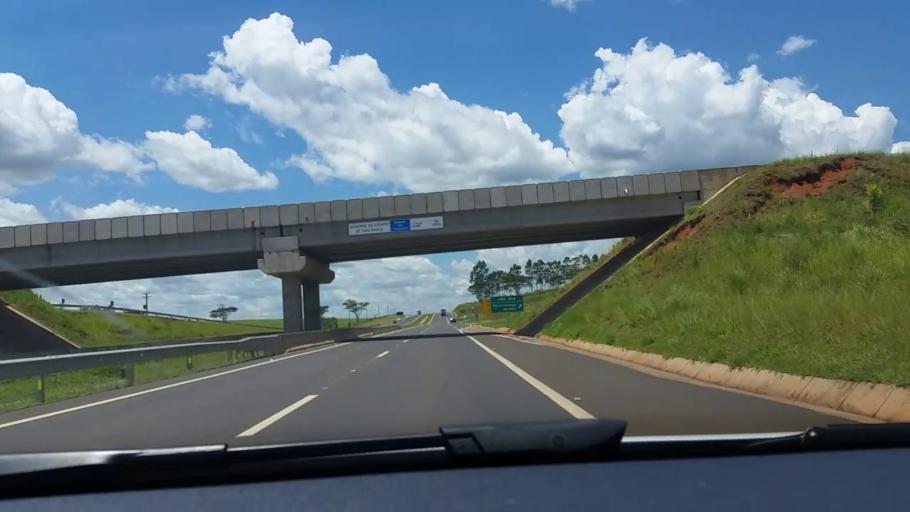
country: BR
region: Sao Paulo
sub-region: Bauru
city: Bauru
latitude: -22.4248
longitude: -49.1253
